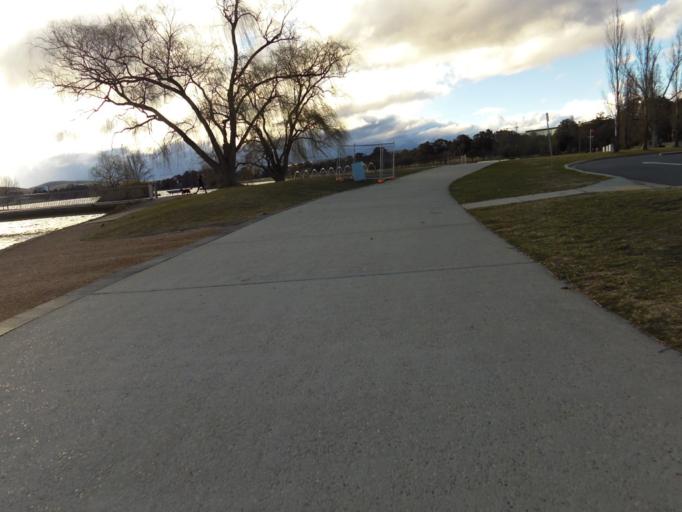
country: AU
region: Australian Capital Territory
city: Canberra
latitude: -35.2987
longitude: 149.1432
